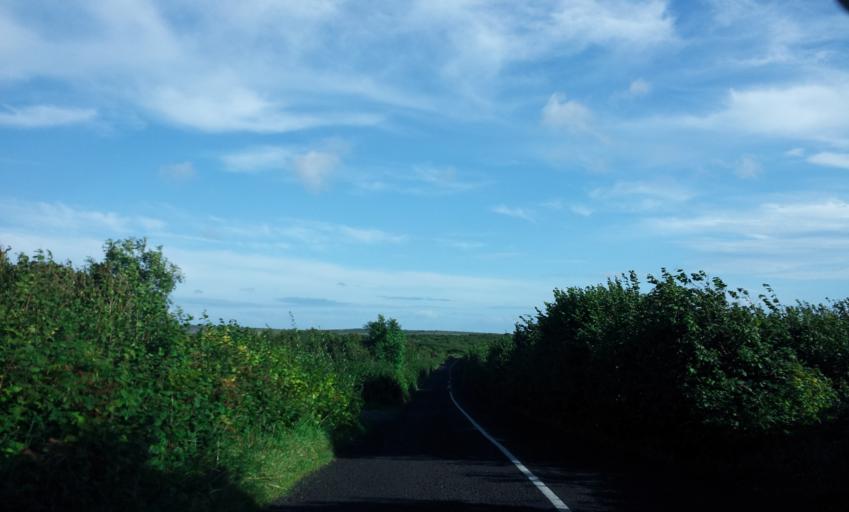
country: IE
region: Munster
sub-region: An Clar
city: Ennis
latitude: 53.0146
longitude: -9.1305
